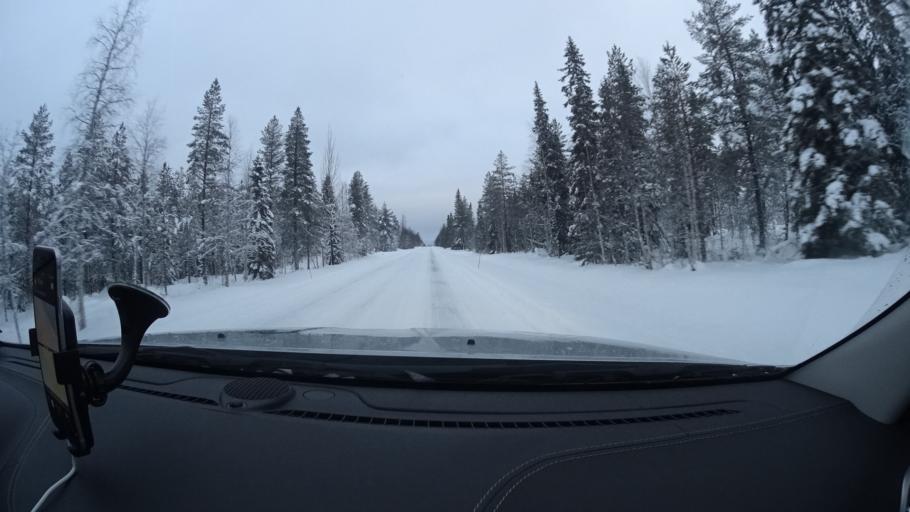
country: FI
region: Lapland
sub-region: Itae-Lappi
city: Posio
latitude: 66.1927
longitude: 27.6658
